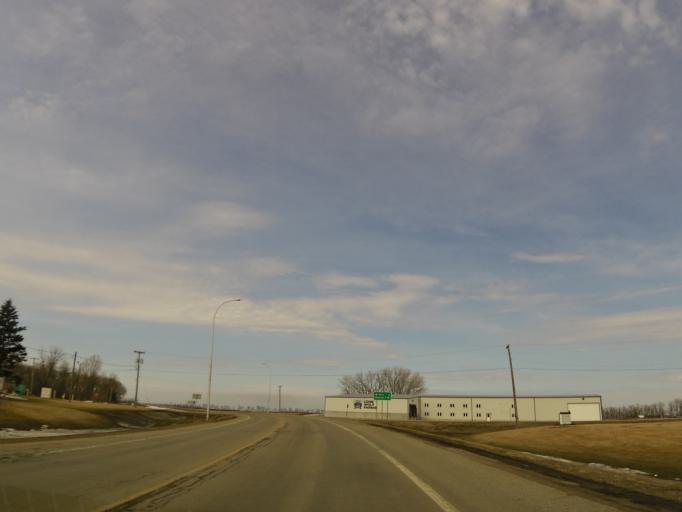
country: US
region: North Dakota
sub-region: Walsh County
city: Grafton
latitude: 48.2949
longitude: -97.3718
